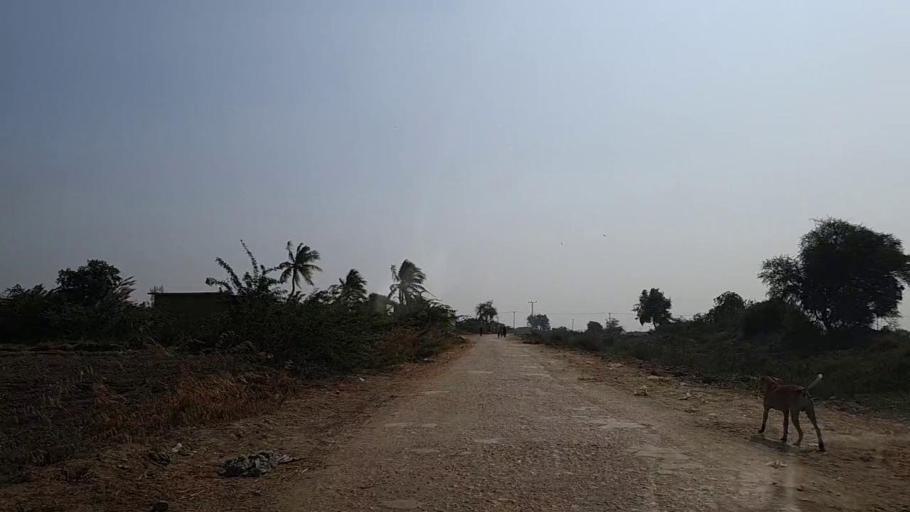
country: PK
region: Sindh
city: Thatta
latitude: 24.7410
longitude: 67.7688
